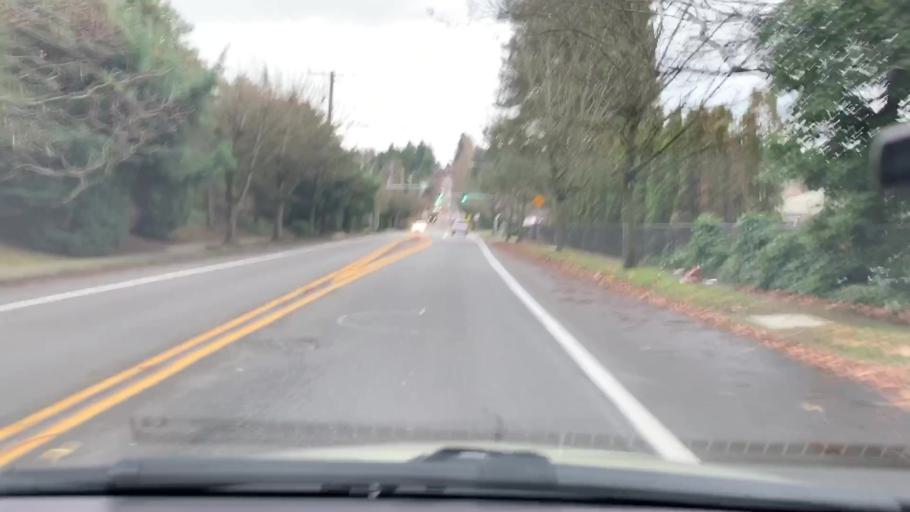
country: US
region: Washington
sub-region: King County
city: Kingsgate
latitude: 47.7183
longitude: -122.1824
